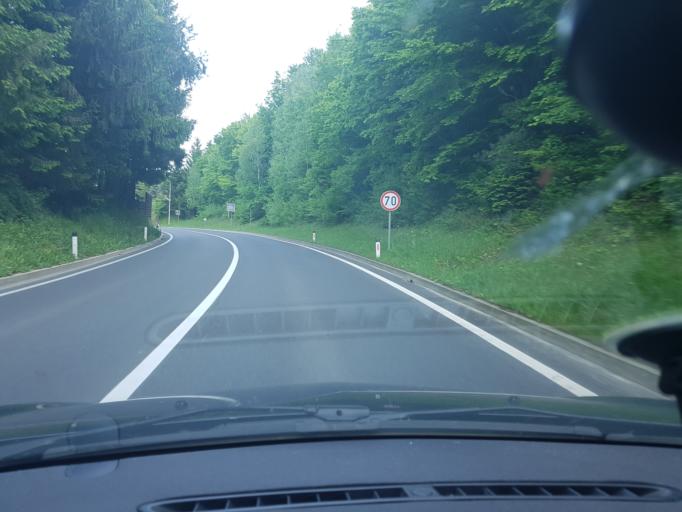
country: SI
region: Rogaska Slatina
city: Rogaska Slatina
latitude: 46.2520
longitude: 15.6277
